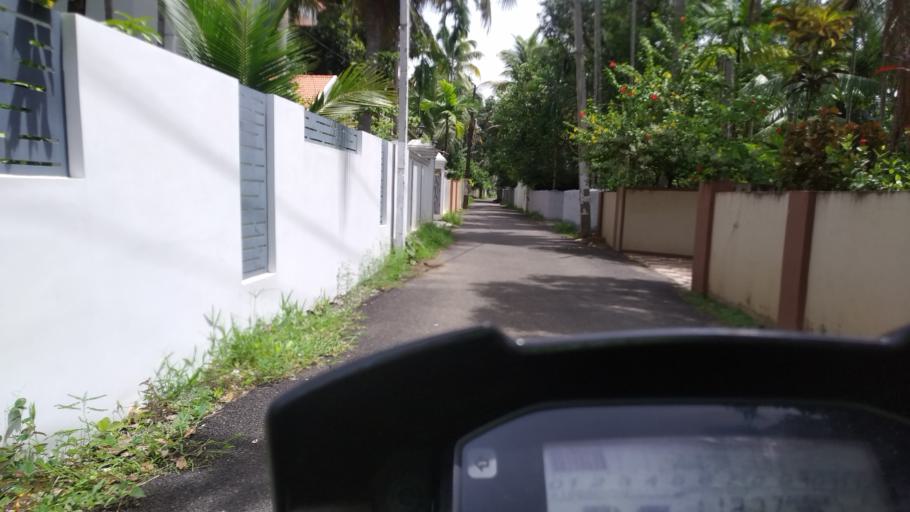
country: IN
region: Kerala
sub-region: Ernakulam
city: Elur
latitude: 10.0818
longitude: 76.2121
